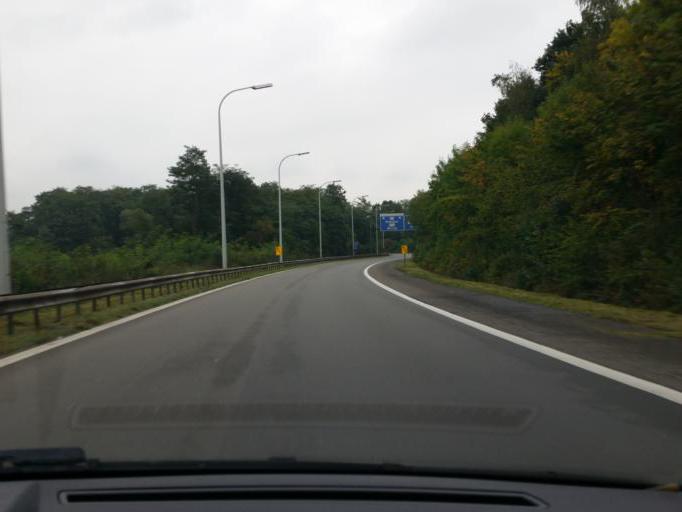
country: BE
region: Flanders
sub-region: Provincie Antwerpen
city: Edegem
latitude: 51.1704
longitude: 4.4147
